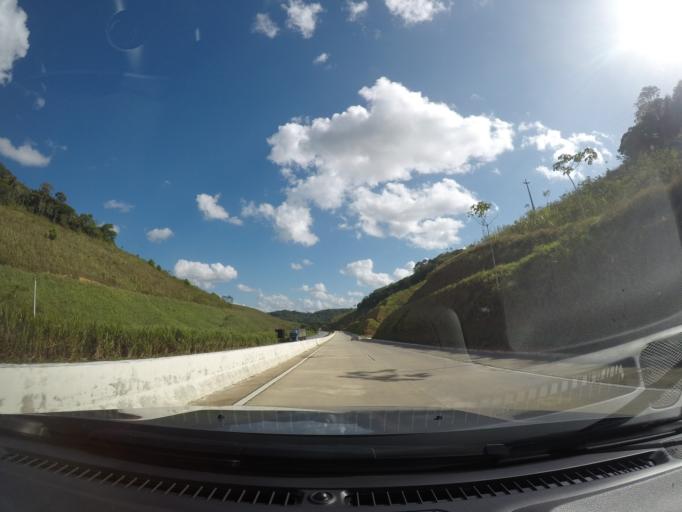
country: BR
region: Pernambuco
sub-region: Palmares
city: Palmares
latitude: -8.7485
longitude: -35.6035
